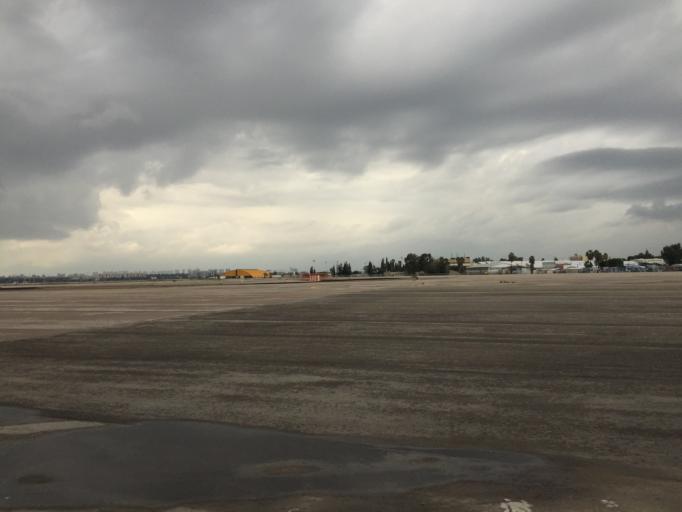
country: IL
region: Central District
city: Yehud
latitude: 31.9960
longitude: 34.8972
